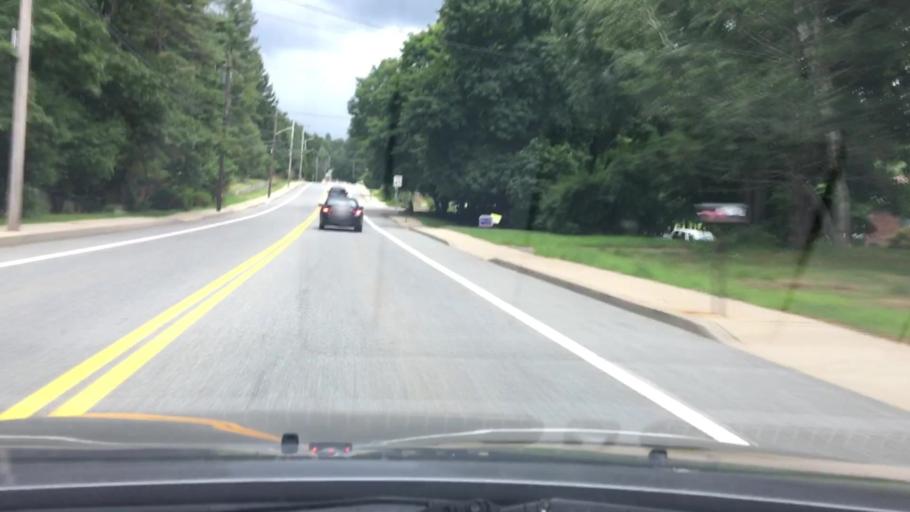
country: US
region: Rhode Island
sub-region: Providence County
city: Cumberland
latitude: 41.9770
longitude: -71.3904
